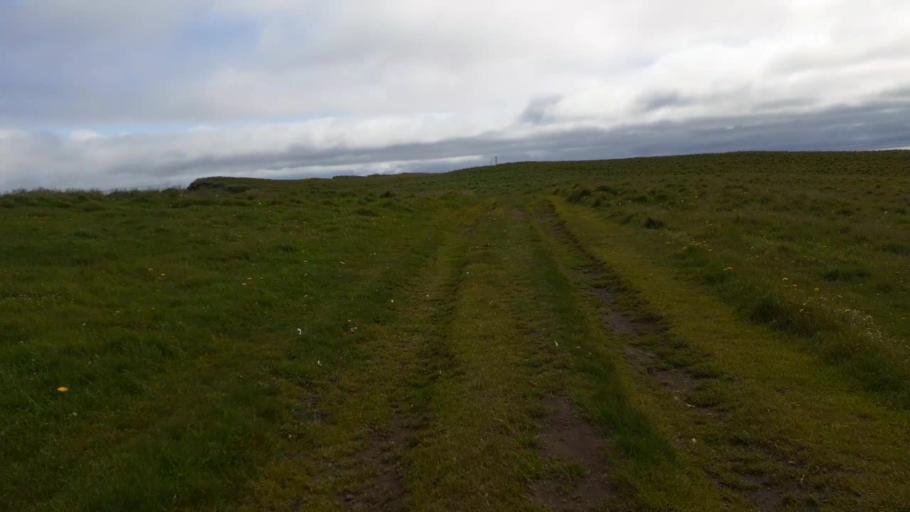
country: IS
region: Northeast
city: Dalvik
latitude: 66.5550
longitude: -18.0018
